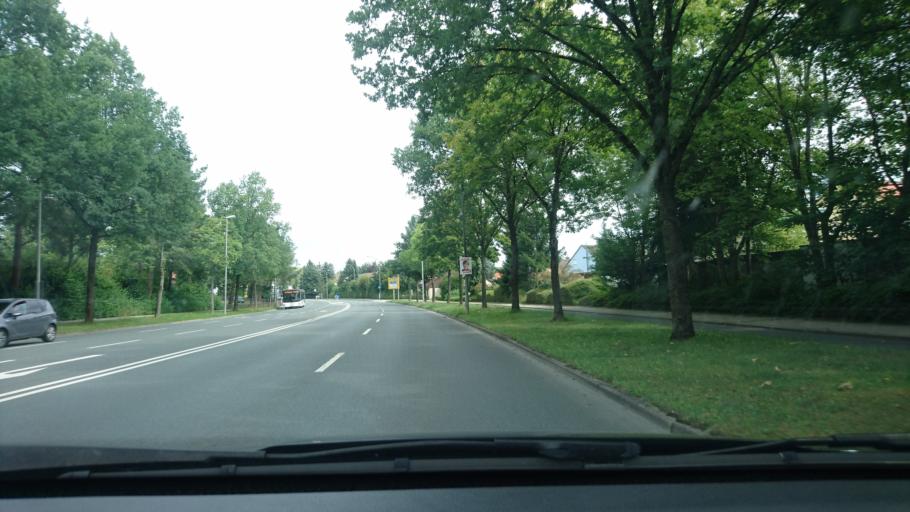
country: DE
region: Bavaria
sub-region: Upper Franconia
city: Heinersreuth
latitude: 49.9440
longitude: 11.5459
